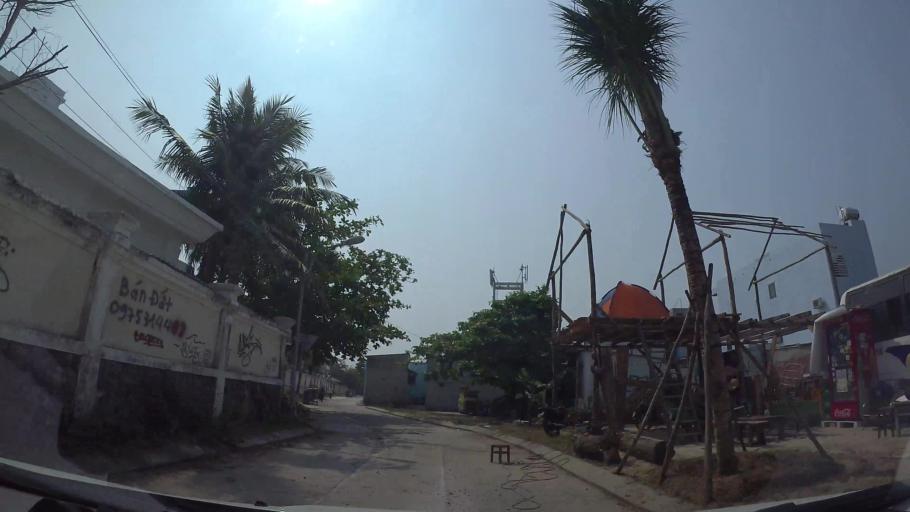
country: VN
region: Da Nang
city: Son Tra
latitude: 16.0467
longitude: 108.2475
